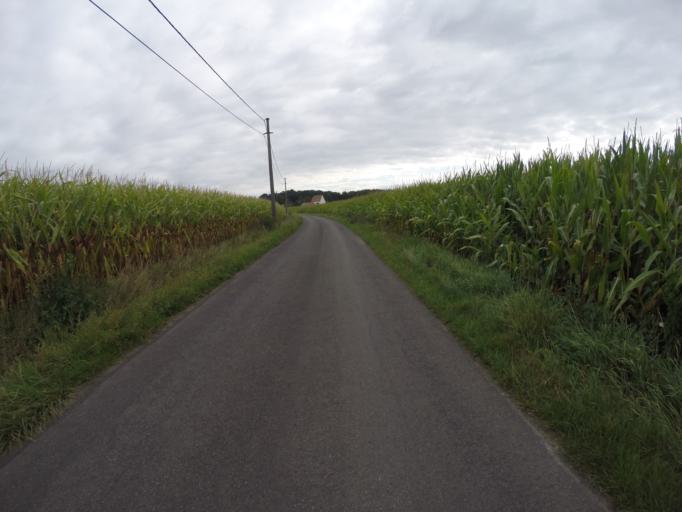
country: BE
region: Flanders
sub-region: Provincie West-Vlaanderen
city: Ruiselede
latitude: 51.0483
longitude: 3.3759
